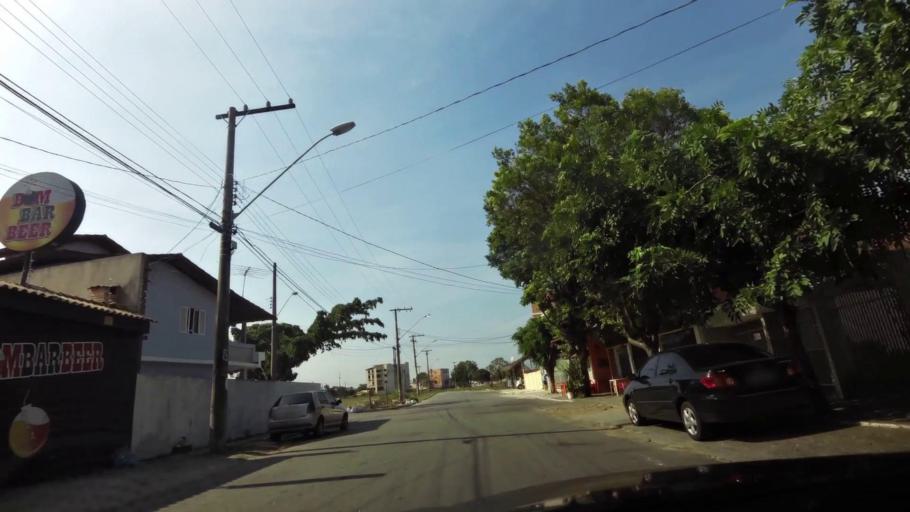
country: BR
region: Espirito Santo
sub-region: Guarapari
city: Guarapari
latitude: -20.6540
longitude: -40.4940
